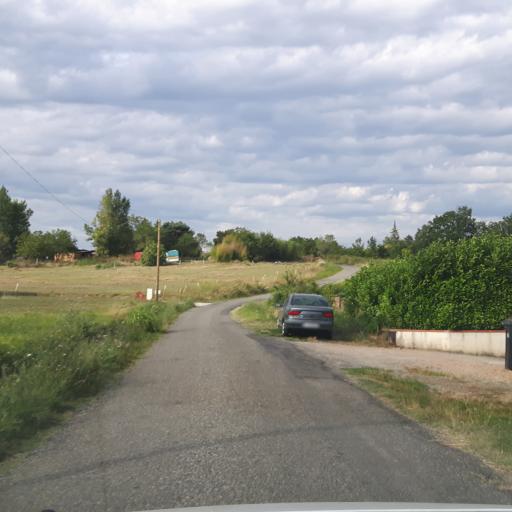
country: FR
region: Midi-Pyrenees
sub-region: Departement de la Haute-Garonne
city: Castelnau-d'Estretefonds
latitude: 43.7869
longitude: 1.3736
